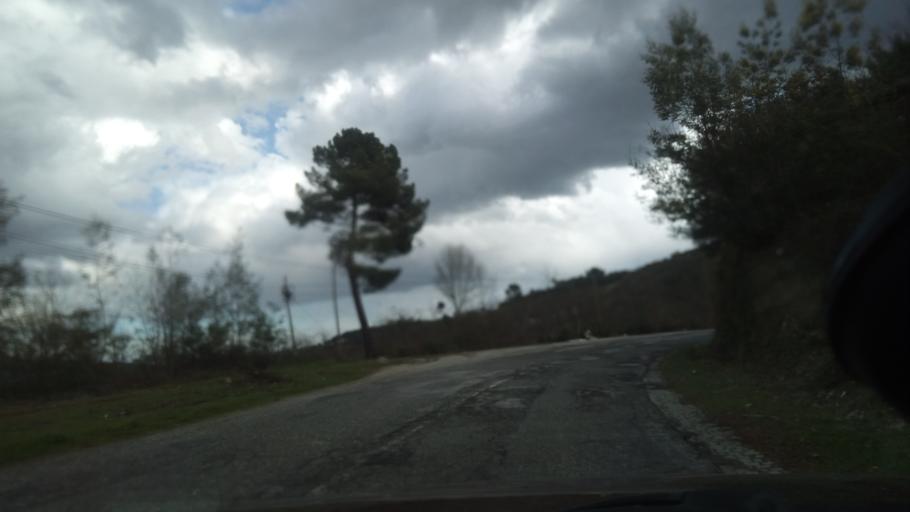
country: PT
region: Guarda
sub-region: Fornos de Algodres
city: Fornos de Algodres
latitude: 40.6281
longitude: -7.4678
